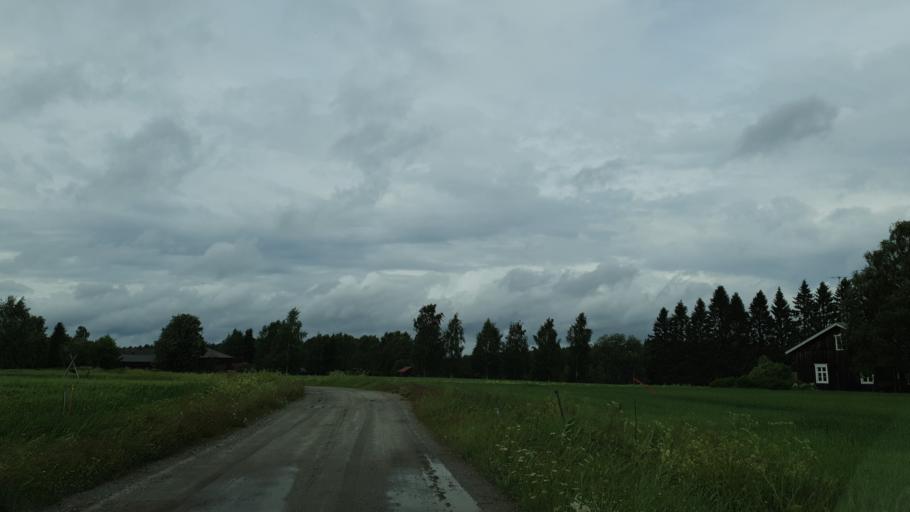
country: FI
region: Kainuu
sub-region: Kehys-Kainuu
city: Kuhmo
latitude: 64.1283
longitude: 29.5740
